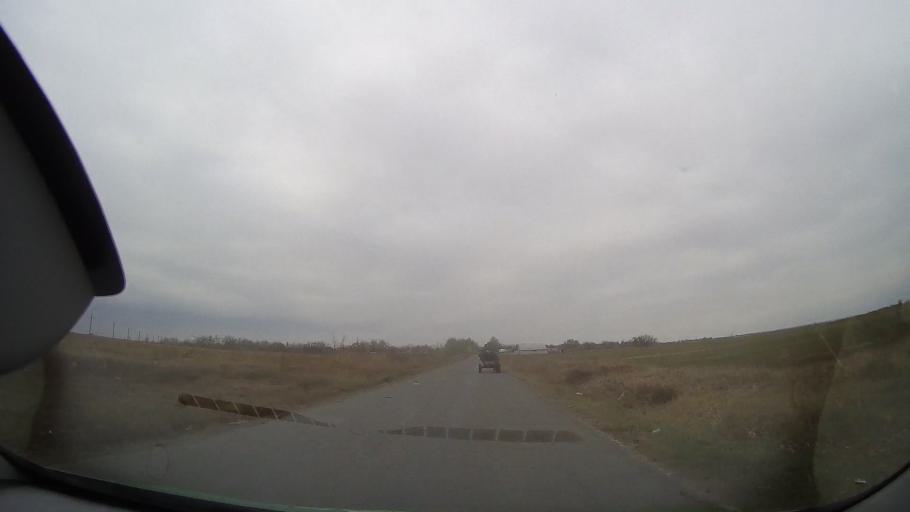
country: RO
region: Buzau
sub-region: Comuna Luciu
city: Luciu
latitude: 44.9676
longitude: 27.0973
